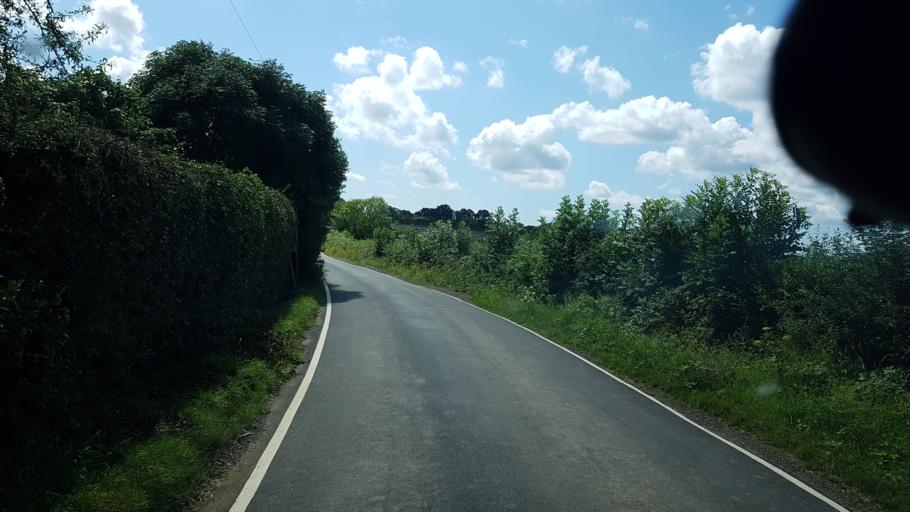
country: GB
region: England
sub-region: Kent
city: Edenbridge
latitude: 51.2174
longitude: 0.1316
